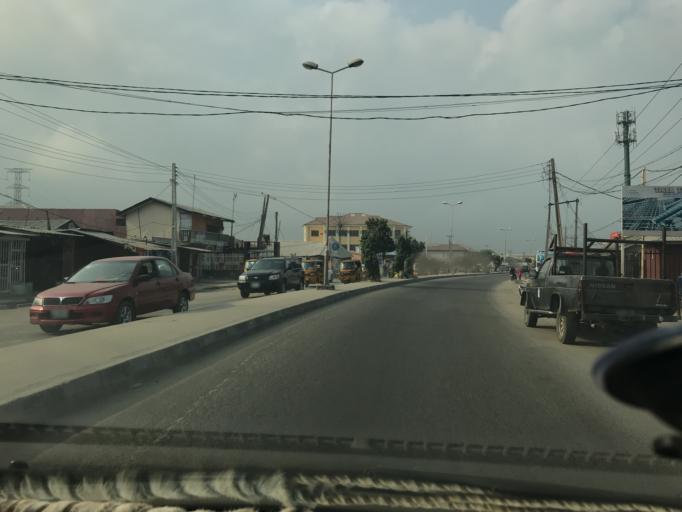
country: NG
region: Lagos
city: Ebute Ikorodu
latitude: 6.4891
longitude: 3.5806
